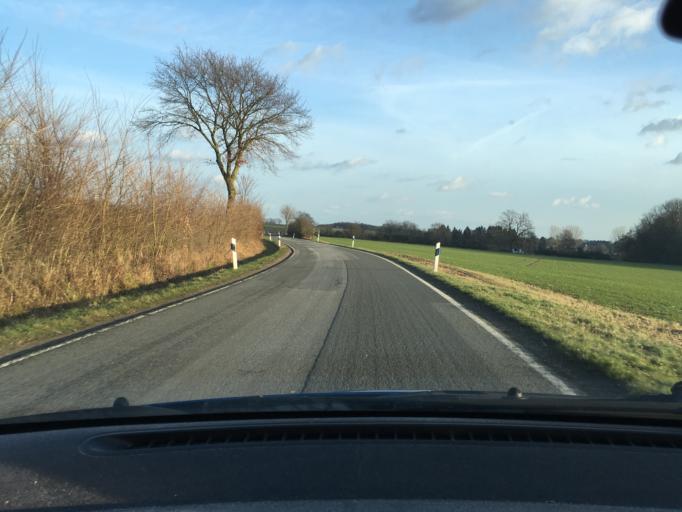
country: DE
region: Schleswig-Holstein
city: Schulendorf
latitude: 53.4607
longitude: 10.5863
